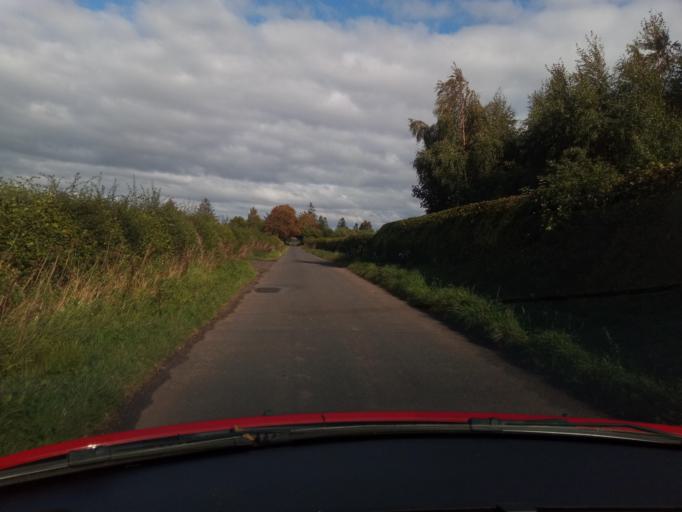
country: GB
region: Scotland
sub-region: The Scottish Borders
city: Kelso
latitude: 55.5607
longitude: -2.4243
